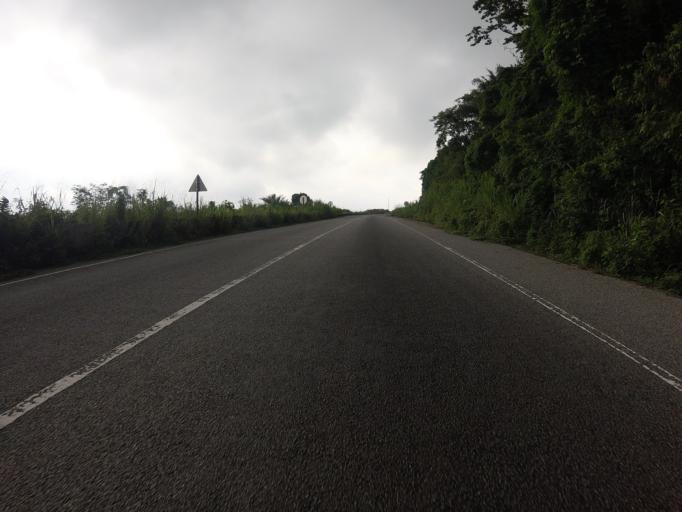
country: GH
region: Volta
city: Ho
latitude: 6.8156
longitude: 0.4225
